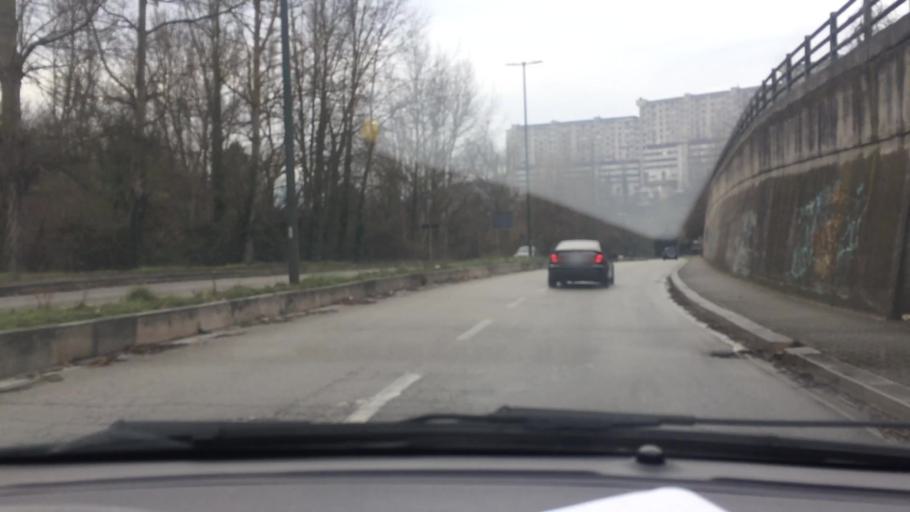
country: IT
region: Basilicate
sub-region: Provincia di Potenza
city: Potenza
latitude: 40.6347
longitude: 15.7951
